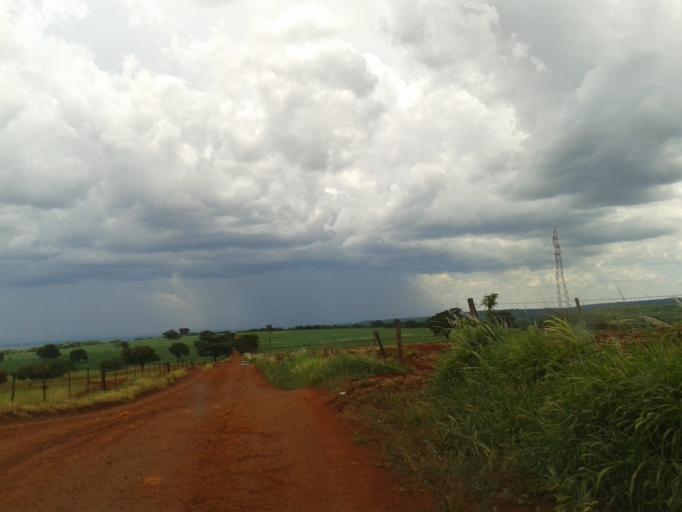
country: BR
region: Minas Gerais
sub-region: Centralina
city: Centralina
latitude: -18.7098
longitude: -49.2152
